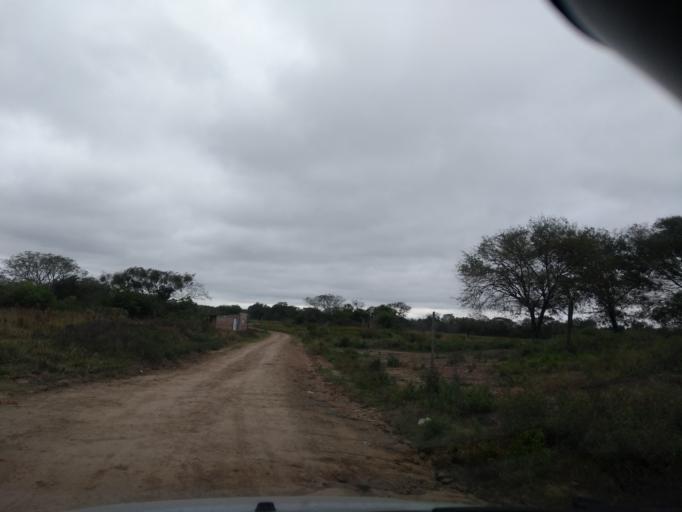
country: AR
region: Chaco
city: Barranqueras
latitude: -27.4369
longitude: -58.9388
